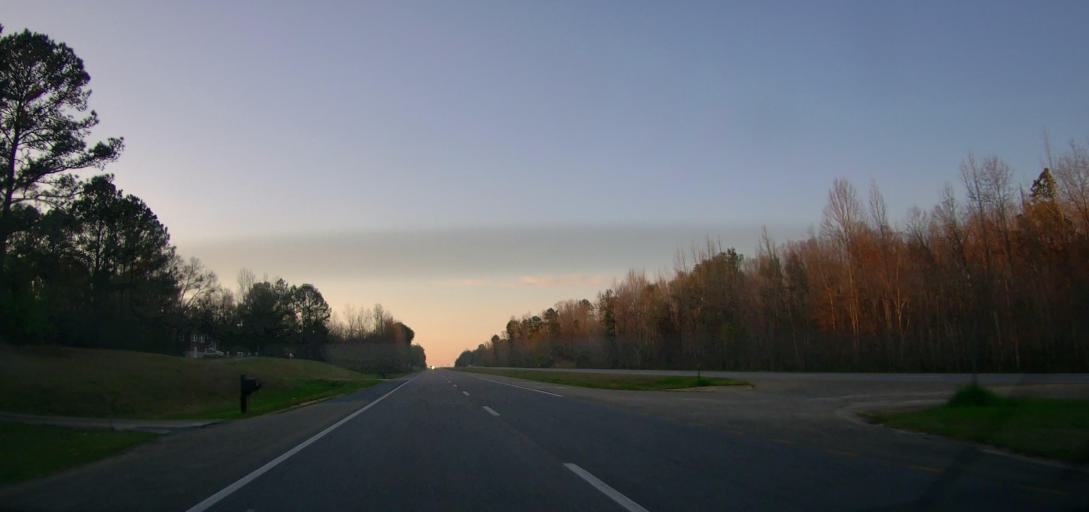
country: US
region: Alabama
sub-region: Coosa County
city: Stewartville
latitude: 33.1176
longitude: -86.2397
